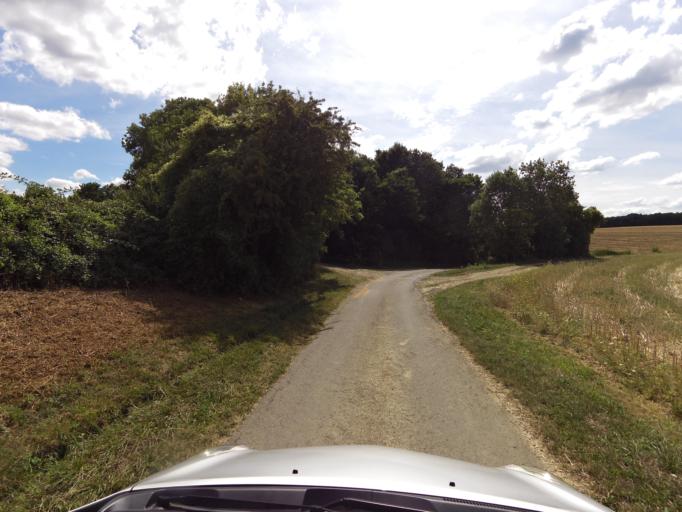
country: FR
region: Picardie
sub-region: Departement de l'Aisne
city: Bruyeres-et-Montberault
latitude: 49.4838
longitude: 3.6463
